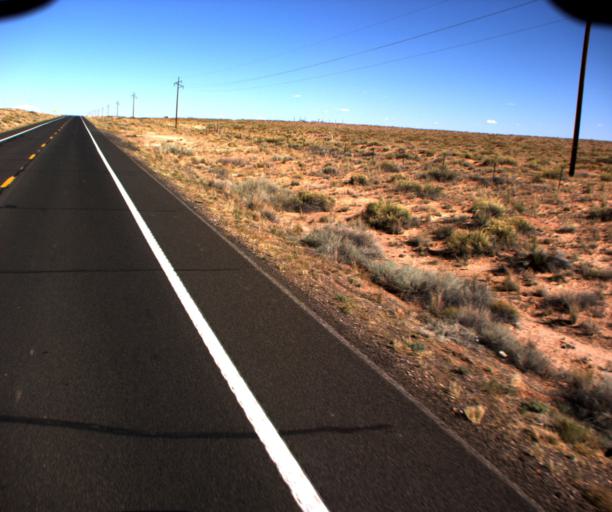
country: US
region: Arizona
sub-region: Coconino County
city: Tuba City
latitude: 36.1383
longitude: -111.1676
